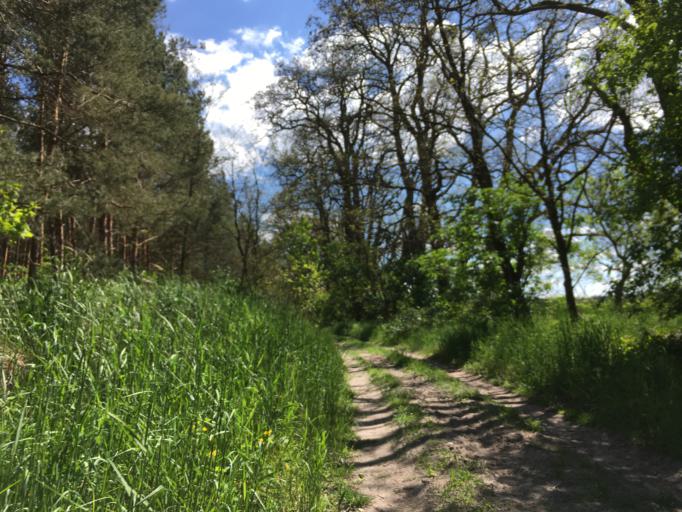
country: DE
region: Brandenburg
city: Rudnitz
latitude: 52.7158
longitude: 13.6573
